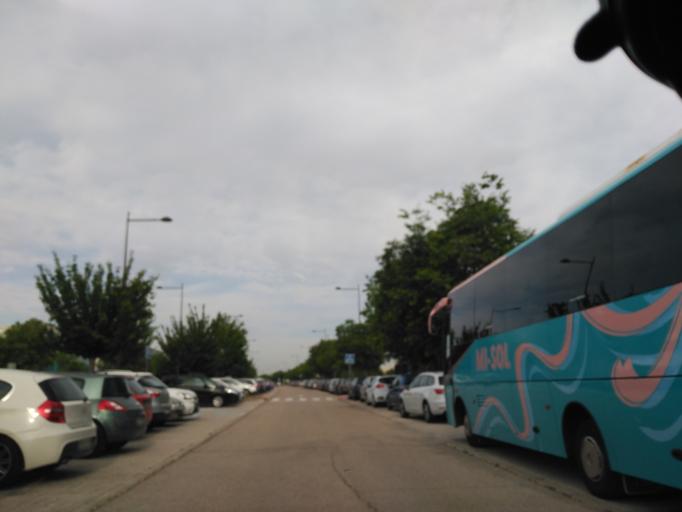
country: ES
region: Madrid
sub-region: Provincia de Madrid
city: Getafe
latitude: 40.2897
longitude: -3.6961
